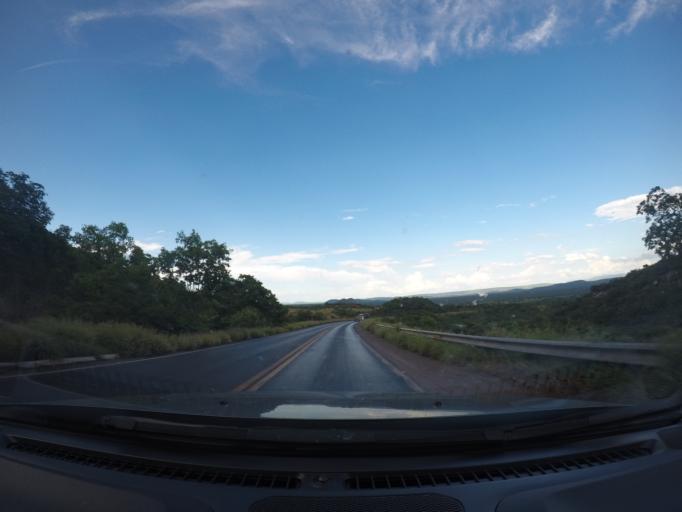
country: BR
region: Bahia
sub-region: Ibotirama
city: Ibotirama
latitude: -12.1324
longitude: -43.3497
